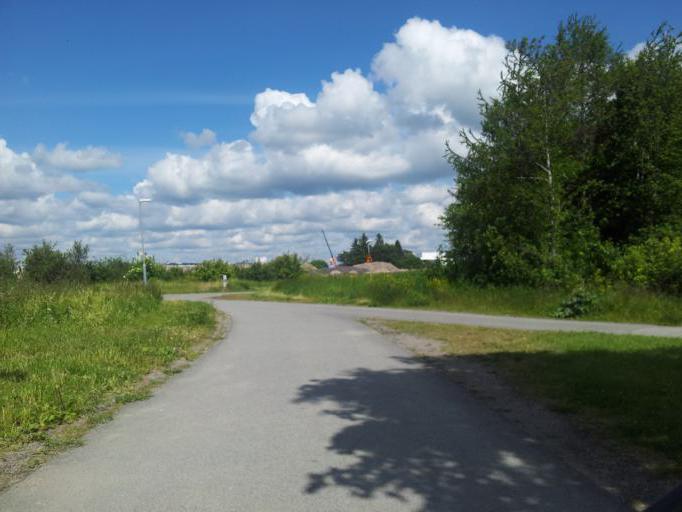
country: SE
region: Uppsala
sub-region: Uppsala Kommun
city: Gamla Uppsala
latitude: 59.8836
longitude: 17.6614
